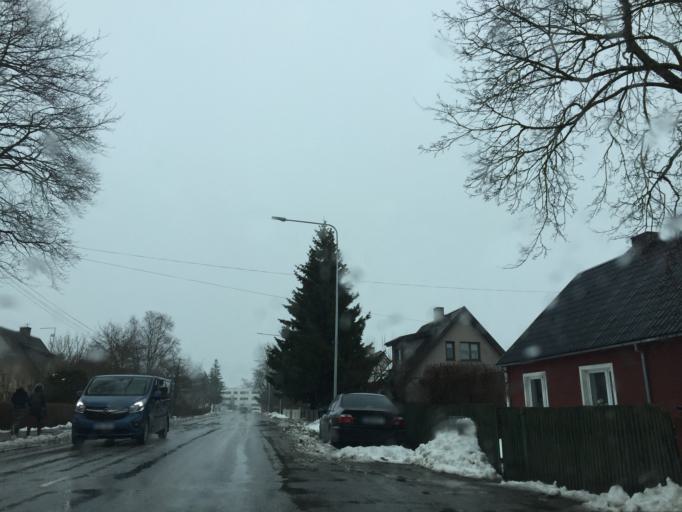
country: EE
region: Saare
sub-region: Kuressaare linn
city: Kuressaare
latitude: 58.2596
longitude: 22.4953
